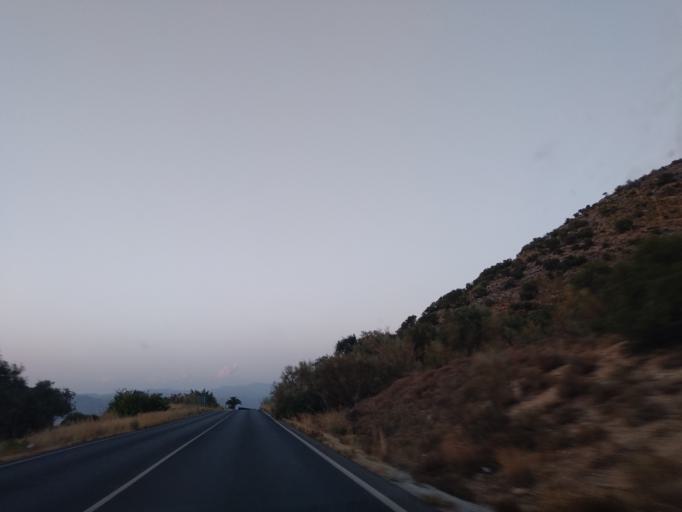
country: ES
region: Andalusia
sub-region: Provincia de Malaga
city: Cartama
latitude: 36.6962
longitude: -4.6509
